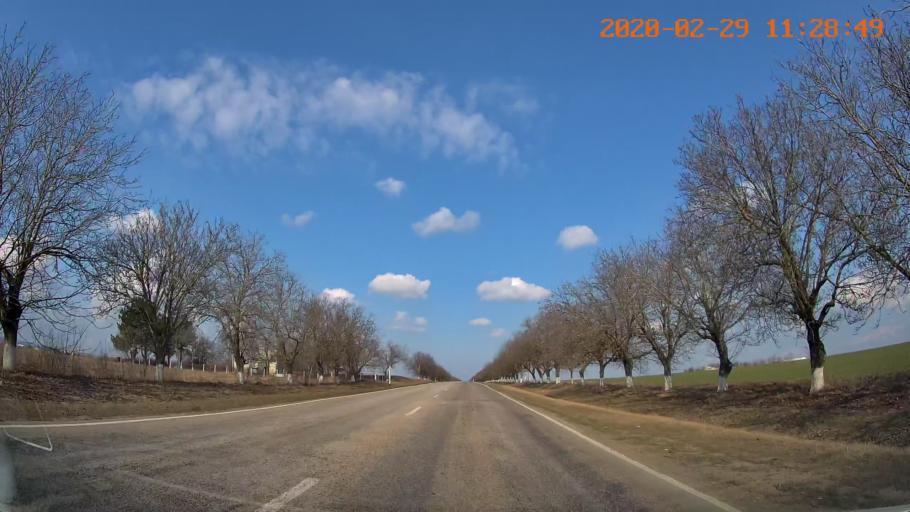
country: MD
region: Telenesti
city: Cocieri
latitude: 47.4849
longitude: 29.1308
